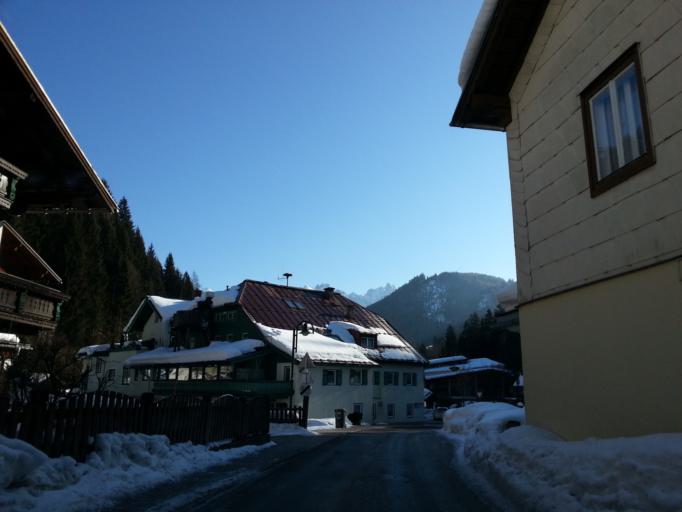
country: AT
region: Salzburg
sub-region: Politischer Bezirk Hallein
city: Abtenau
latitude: 47.4939
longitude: 13.3983
